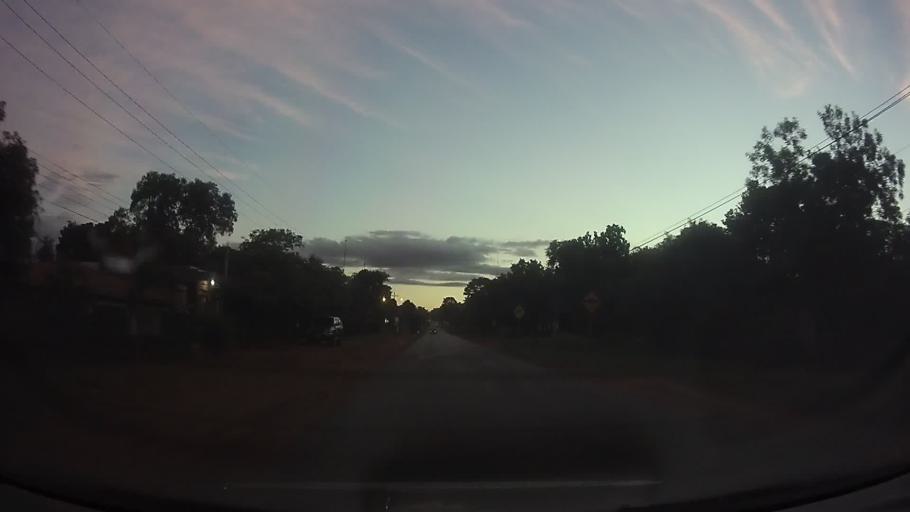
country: PY
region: Central
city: Ita
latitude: -25.4360
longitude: -57.3672
